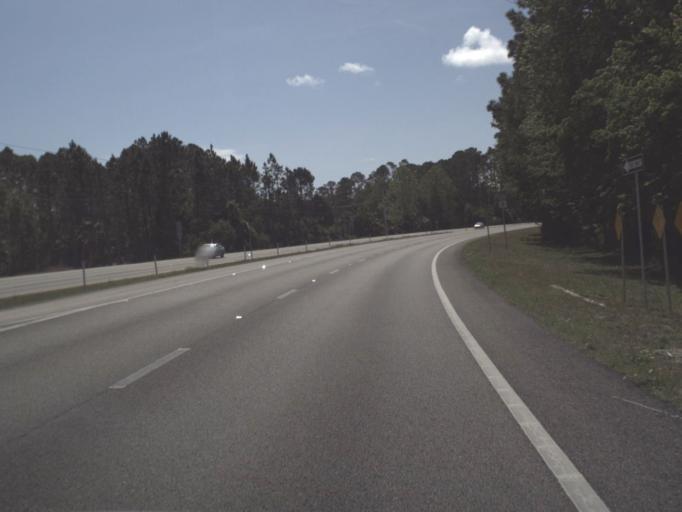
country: US
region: Florida
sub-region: Flagler County
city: Bunnell
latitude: 29.4067
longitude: -81.1970
